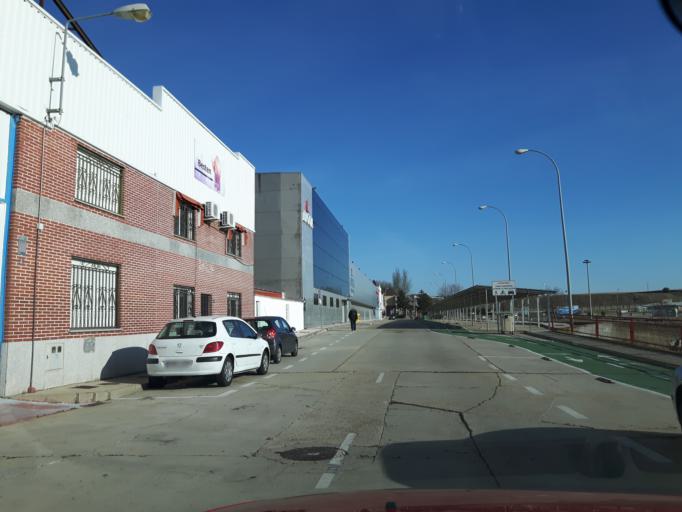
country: ES
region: Castille and Leon
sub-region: Provincia de Salamanca
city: Villares de la Reina
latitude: 40.9894
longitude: -5.6484
